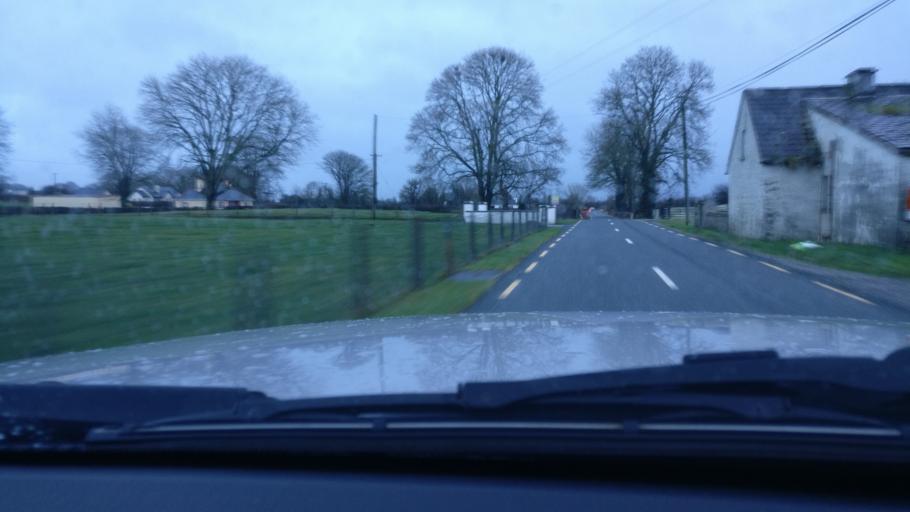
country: IE
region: Connaught
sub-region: County Galway
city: Ballinasloe
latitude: 53.2294
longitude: -8.3159
